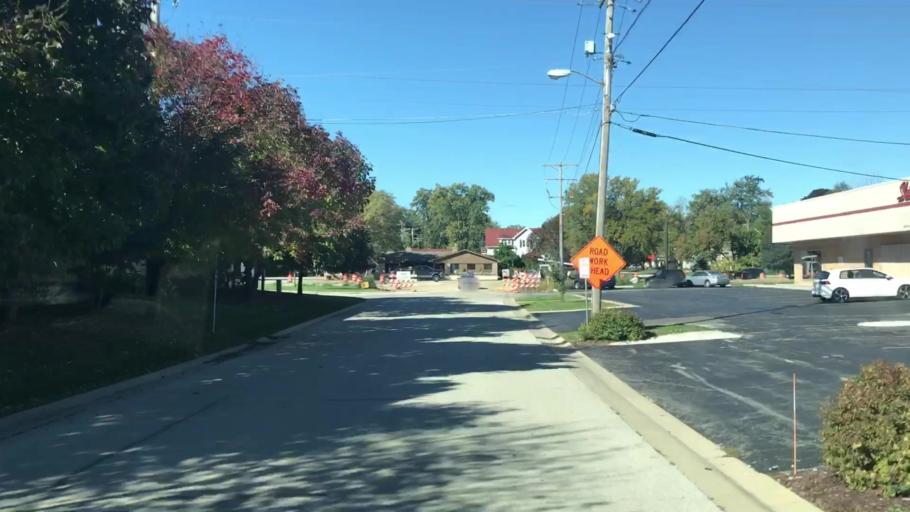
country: US
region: Wisconsin
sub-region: Milwaukee County
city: Hales Corners
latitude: 42.9397
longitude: -88.0471
